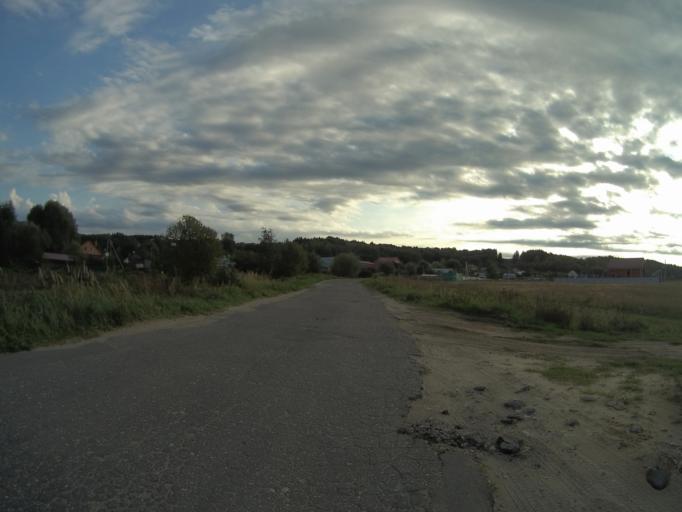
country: RU
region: Vladimir
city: Raduzhnyy
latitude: 56.0179
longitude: 40.3481
